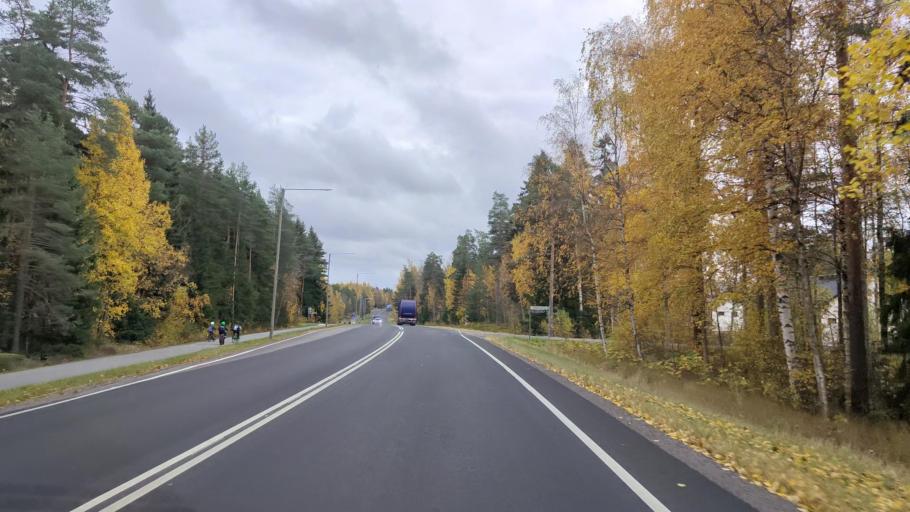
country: FI
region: Varsinais-Suomi
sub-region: Turku
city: Kaarina
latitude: 60.4561
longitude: 22.3669
